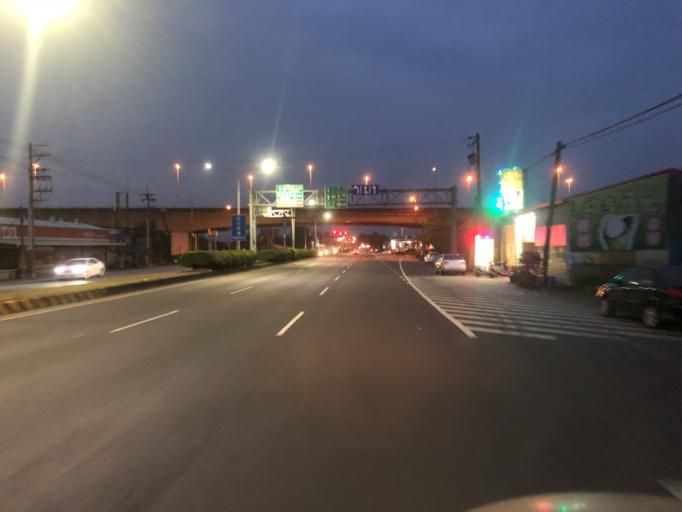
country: TW
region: Taiwan
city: Yujing
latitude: 23.1620
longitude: 120.3412
